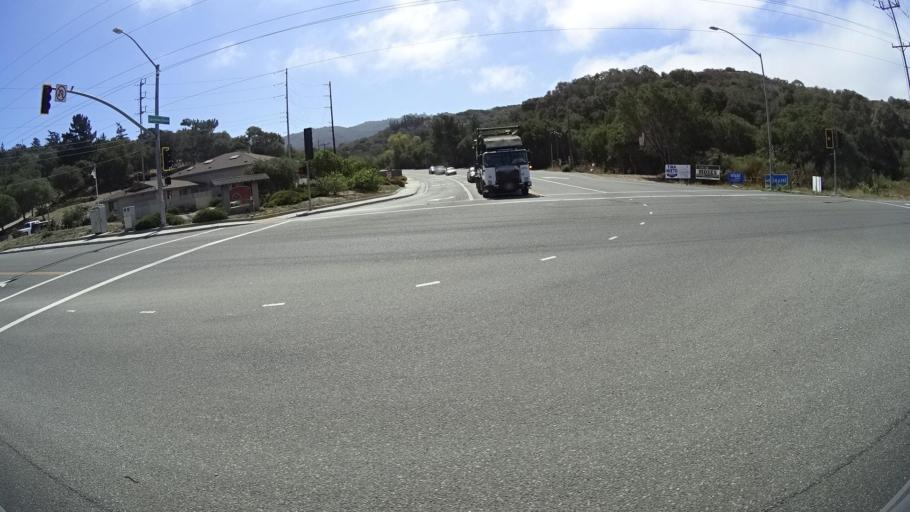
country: US
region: California
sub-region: Monterey County
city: Carmel Valley Village
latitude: 36.5700
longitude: -121.7555
